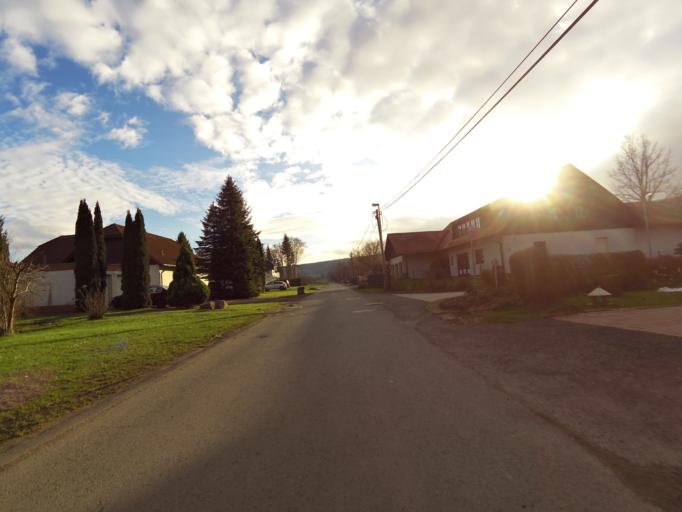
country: DE
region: Lower Saxony
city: Buhren
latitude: 51.4878
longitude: 9.6034
